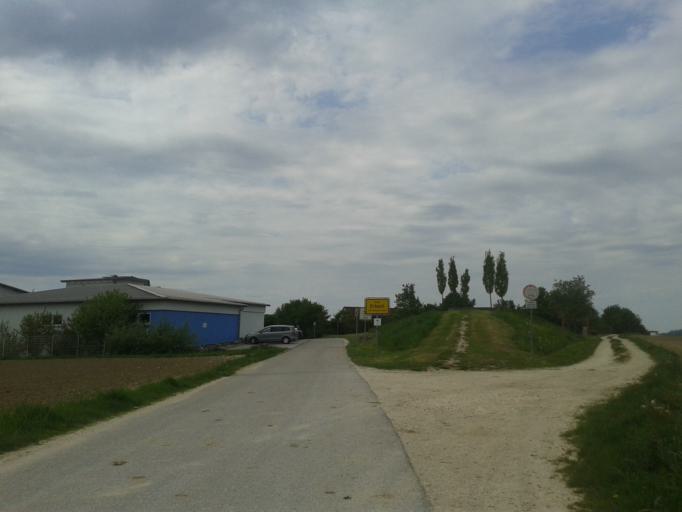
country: DE
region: Baden-Wuerttemberg
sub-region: Tuebingen Region
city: Erbach
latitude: 48.3368
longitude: 9.8992
